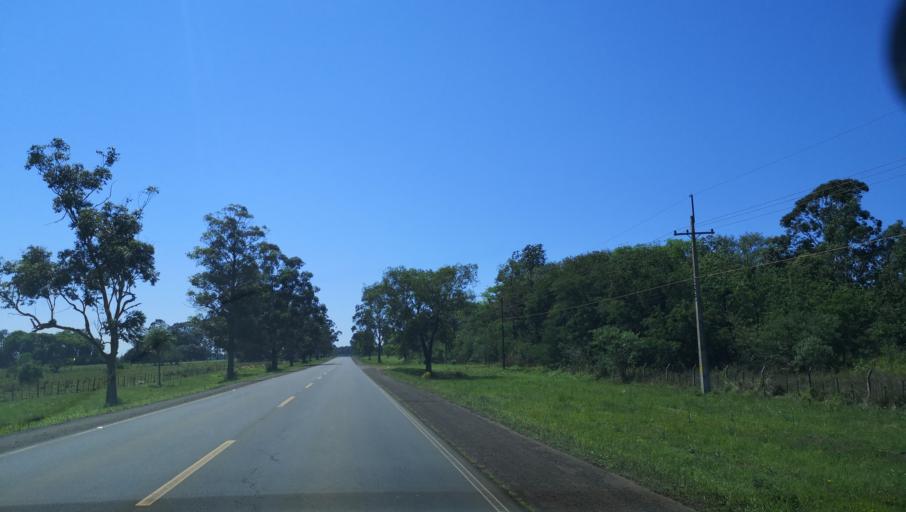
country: PY
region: Itapua
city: Carmen del Parana
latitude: -27.2214
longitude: -56.1144
